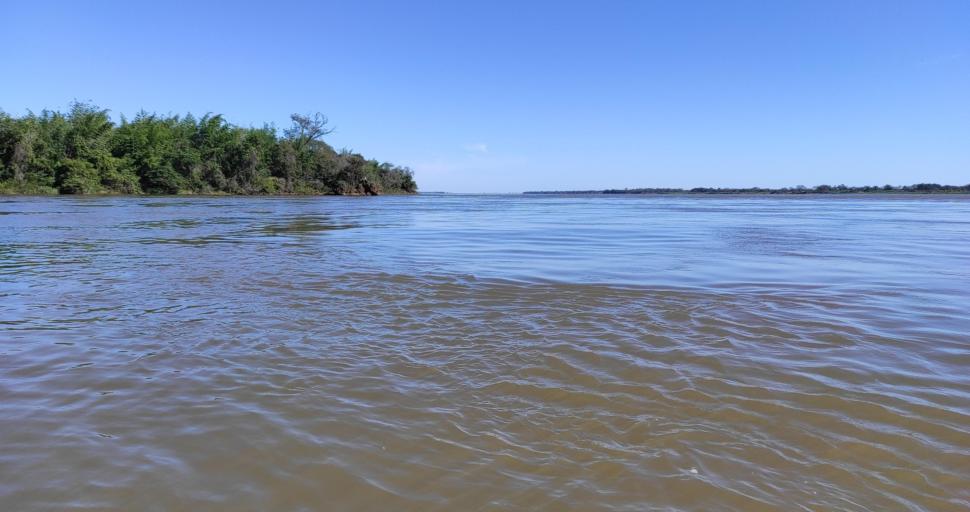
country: AR
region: Corrientes
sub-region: Departamento de Itati
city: Itati
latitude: -27.2797
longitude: -58.3235
